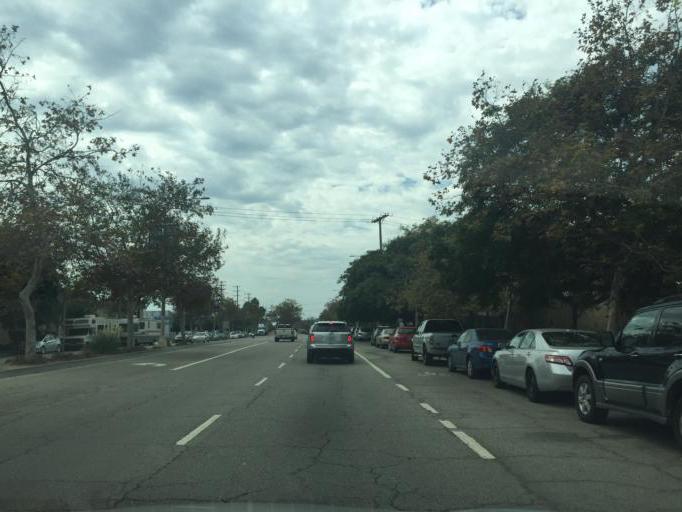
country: US
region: California
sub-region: Los Angeles County
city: Marina del Rey
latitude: 33.9906
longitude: -118.4599
